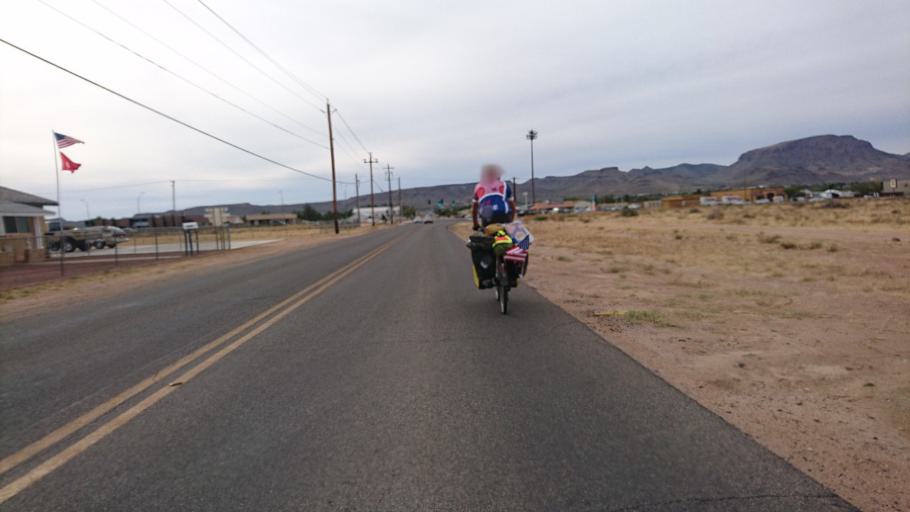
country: US
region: Arizona
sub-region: Mohave County
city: New Kingman-Butler
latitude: 35.2394
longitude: -114.0094
